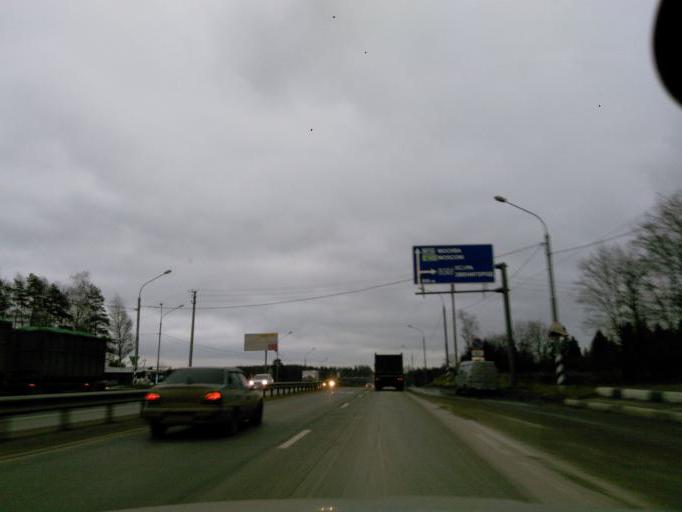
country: RU
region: Moskovskaya
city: Radumlya
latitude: 56.0689
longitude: 37.1352
